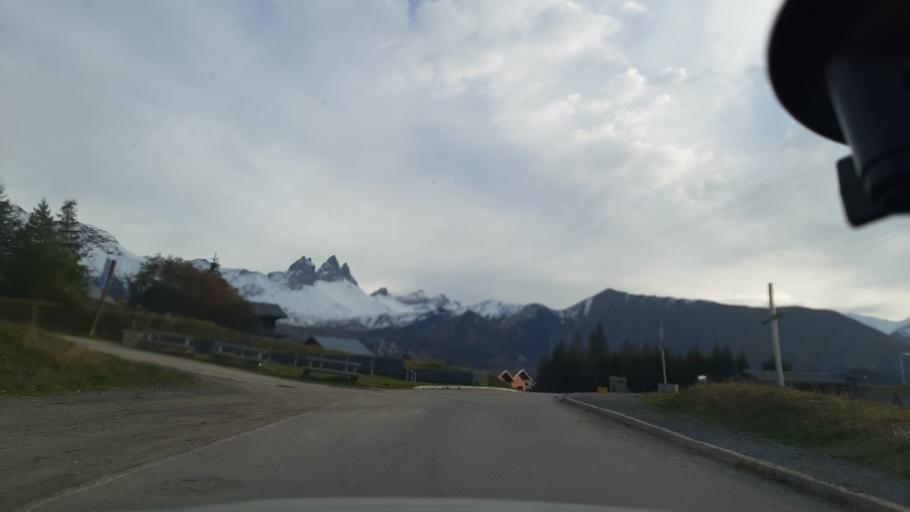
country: FR
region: Rhone-Alpes
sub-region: Departement de la Savoie
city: Villargondran
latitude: 45.2109
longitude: 6.3374
